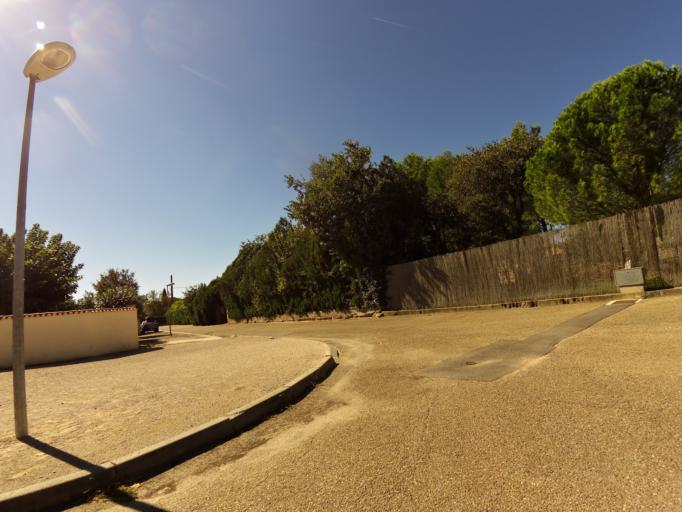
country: FR
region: Languedoc-Roussillon
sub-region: Departement du Gard
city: Codognan
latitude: 43.7334
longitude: 4.2221
